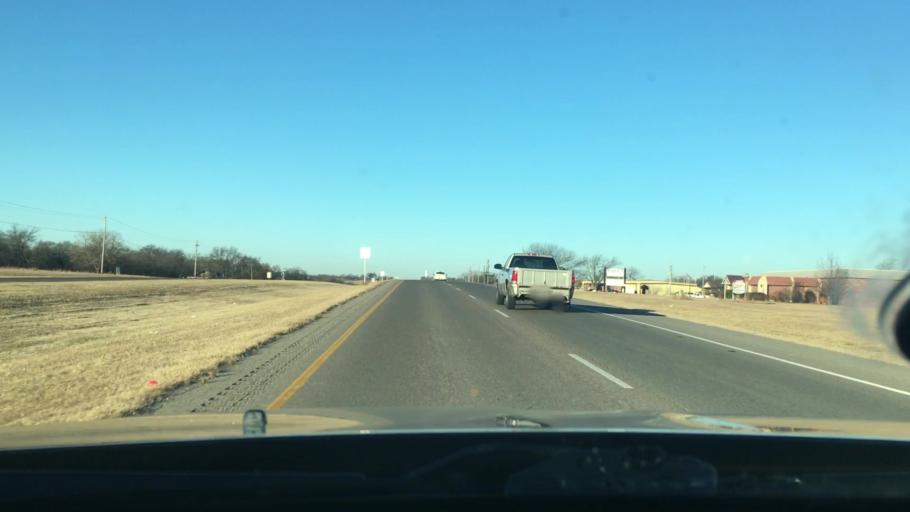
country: US
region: Oklahoma
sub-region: Murray County
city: Sulphur
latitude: 34.5063
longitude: -97.0172
